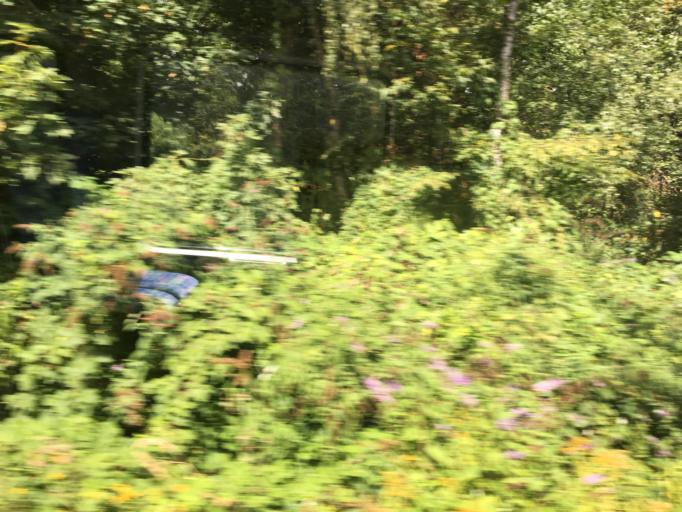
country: DE
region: North Rhine-Westphalia
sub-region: Regierungsbezirk Arnsberg
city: Bochum
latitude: 51.4851
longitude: 7.2565
